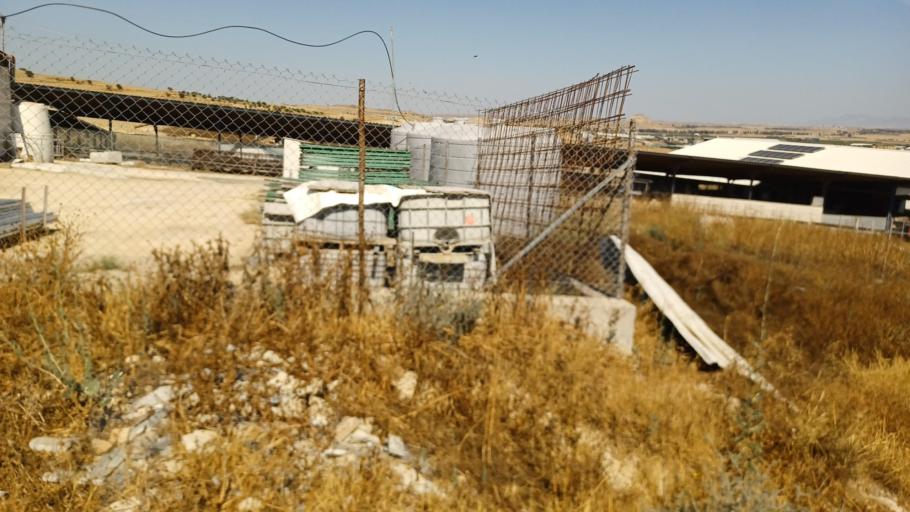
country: CY
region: Larnaka
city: Athienou
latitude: 35.0440
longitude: 33.5306
